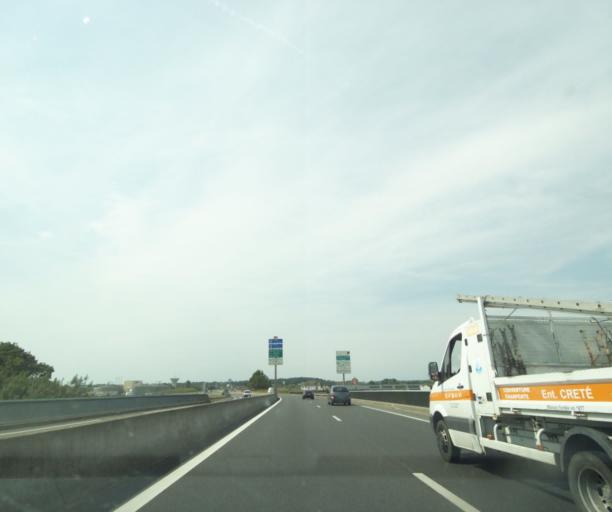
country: FR
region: Centre
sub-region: Departement d'Indre-et-Loire
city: La Riche
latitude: 47.3749
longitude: 0.6522
